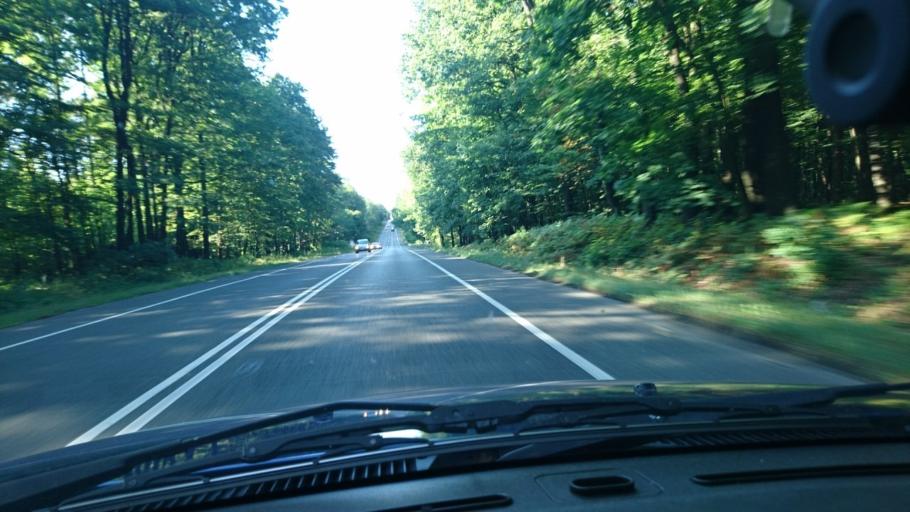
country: PL
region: Silesian Voivodeship
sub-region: Gliwice
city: Gliwice
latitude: 50.3314
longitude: 18.6578
